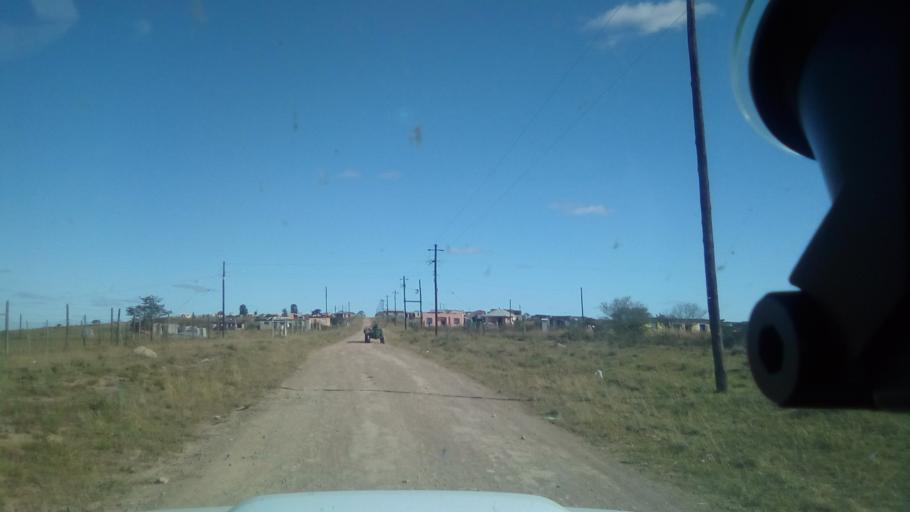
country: ZA
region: Eastern Cape
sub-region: Buffalo City Metropolitan Municipality
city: Bhisho
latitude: -32.7845
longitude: 27.3315
